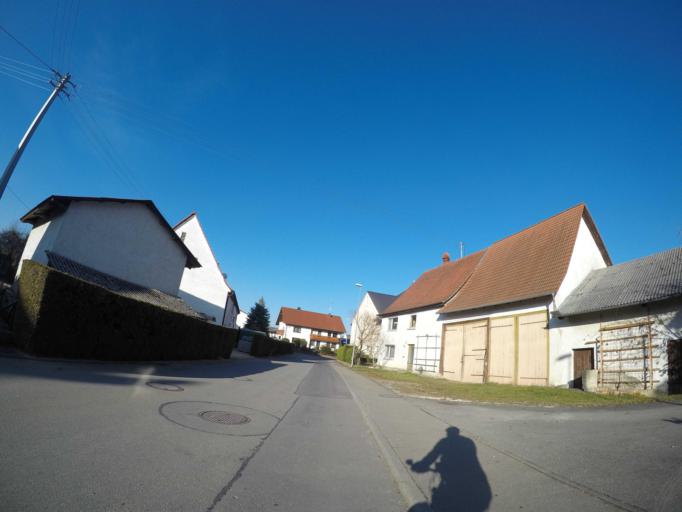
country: DE
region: Baden-Wuerttemberg
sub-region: Tuebingen Region
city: Grundsheim
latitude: 48.1748
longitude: 9.6671
